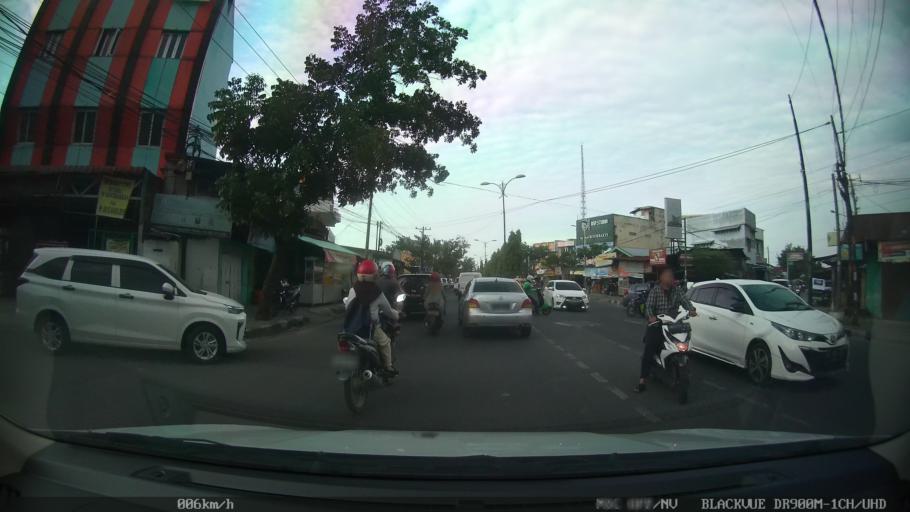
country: ID
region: North Sumatra
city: Sunggal
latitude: 3.5587
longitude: 98.6354
